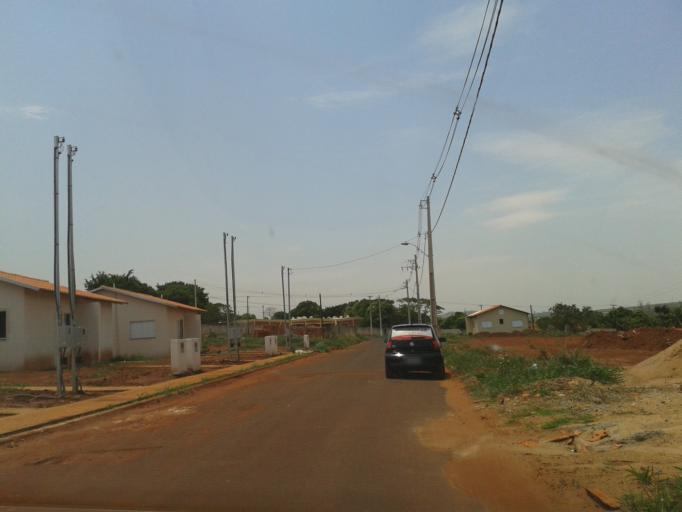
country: BR
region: Minas Gerais
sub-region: Ituiutaba
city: Ituiutaba
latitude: -18.9890
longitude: -49.4370
